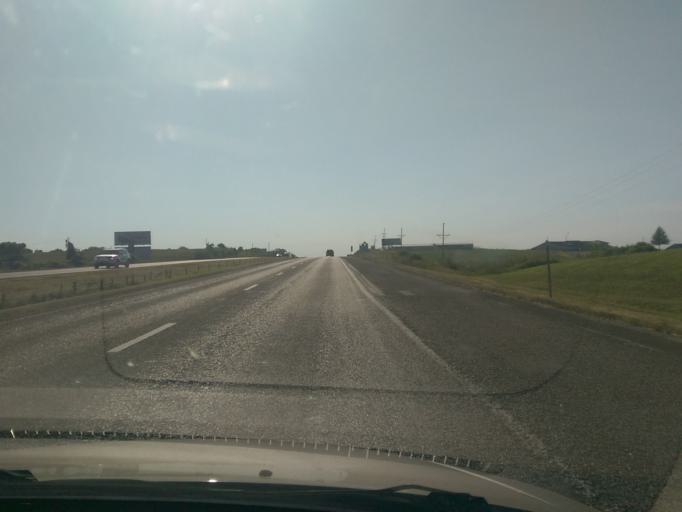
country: US
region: Missouri
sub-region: Lafayette County
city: Concordia
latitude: 38.9926
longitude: -93.5733
